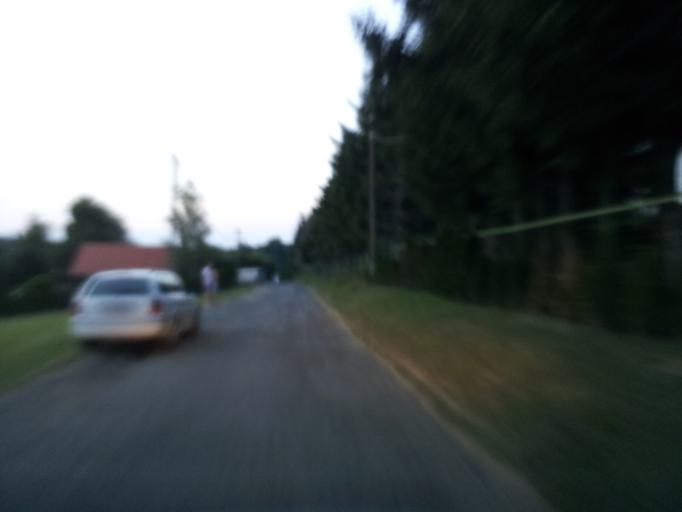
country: HU
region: Zala
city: Zalalovo
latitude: 46.8513
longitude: 16.5701
